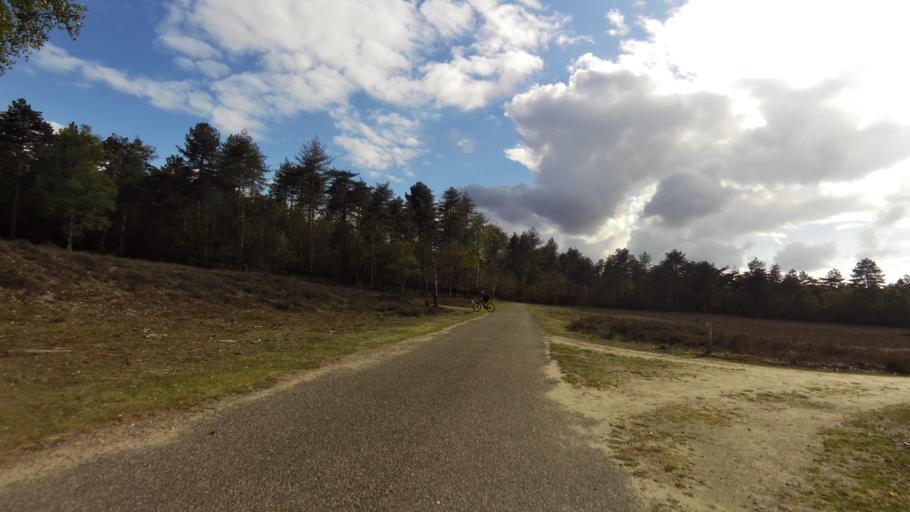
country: NL
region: Gelderland
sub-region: Gemeente Apeldoorn
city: Loenen
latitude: 52.0990
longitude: 5.9789
